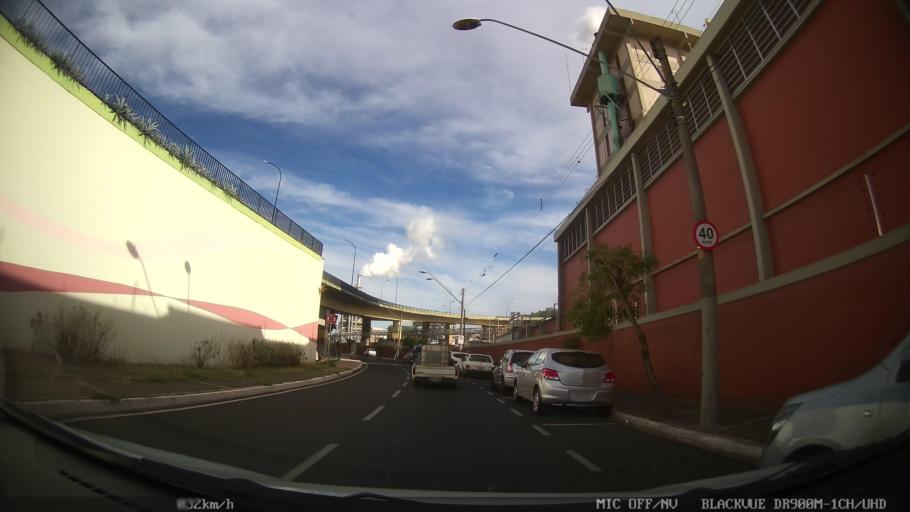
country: BR
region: Sao Paulo
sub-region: Catanduva
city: Catanduva
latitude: -21.1314
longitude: -48.9735
